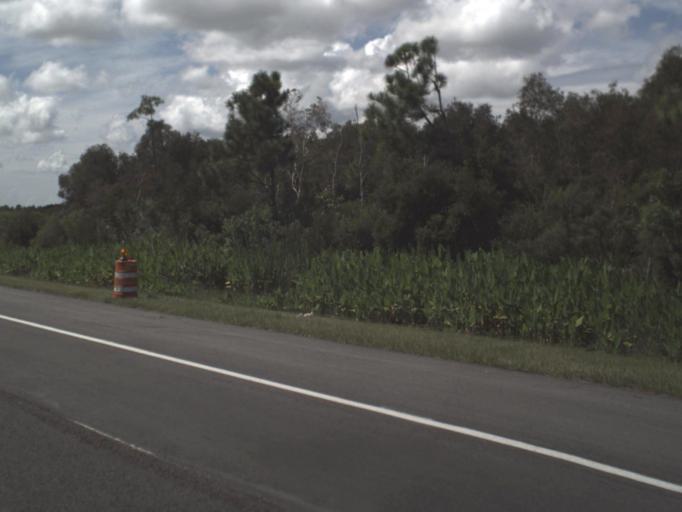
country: US
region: Florida
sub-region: Lee County
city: Gateway
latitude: 26.5410
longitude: -81.7951
